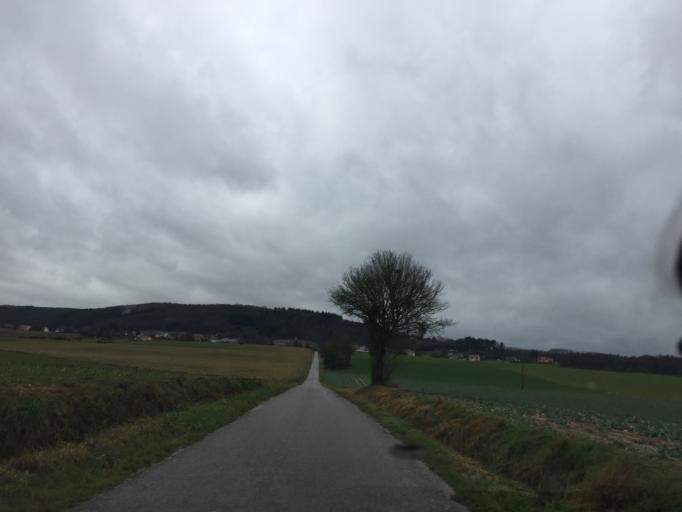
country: FR
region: Franche-Comte
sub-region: Departement du Jura
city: Orchamps
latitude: 47.2019
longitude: 5.6312
